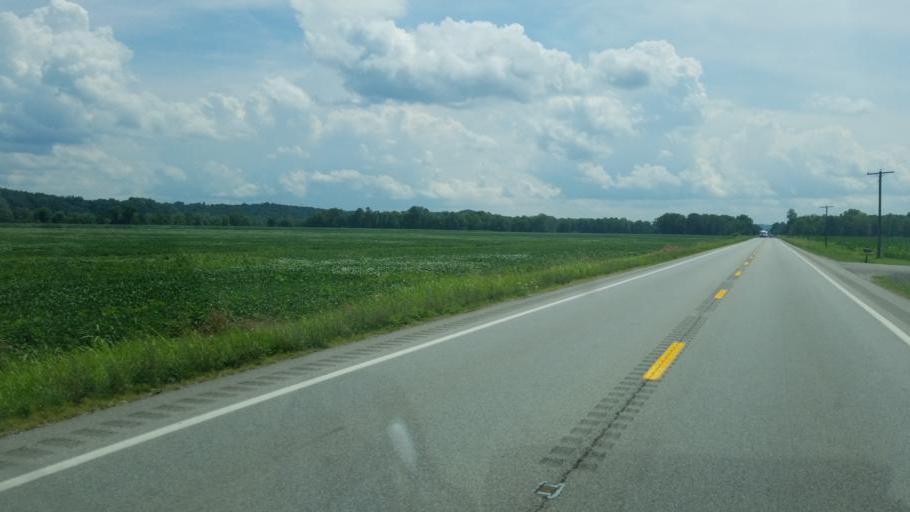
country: US
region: West Virginia
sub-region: Putnam County
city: Buffalo
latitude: 38.6980
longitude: -81.9661
